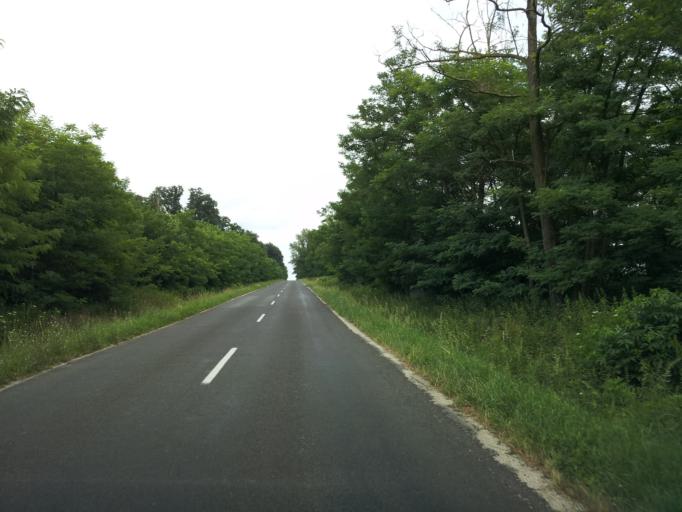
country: HU
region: Zala
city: Turje
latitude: 47.0422
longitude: 16.9914
